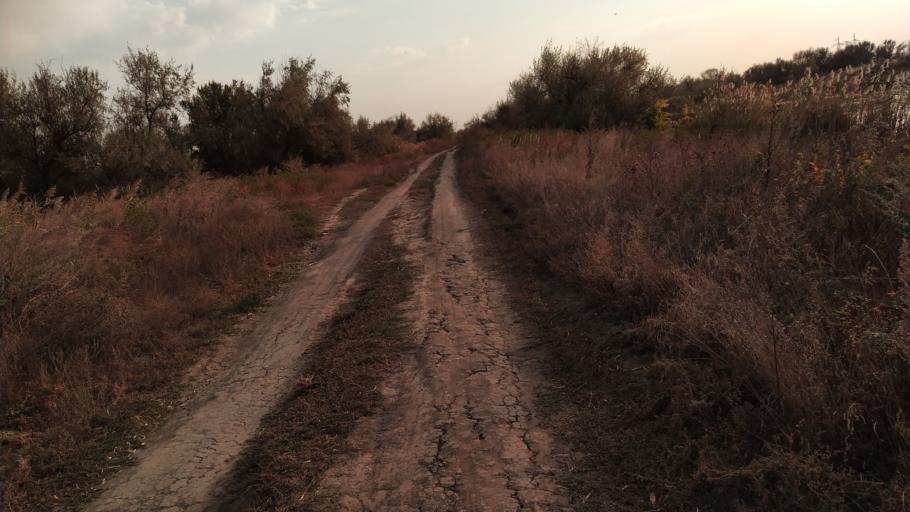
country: RU
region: Rostov
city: Kuleshovka
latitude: 47.1205
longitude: 39.6033
